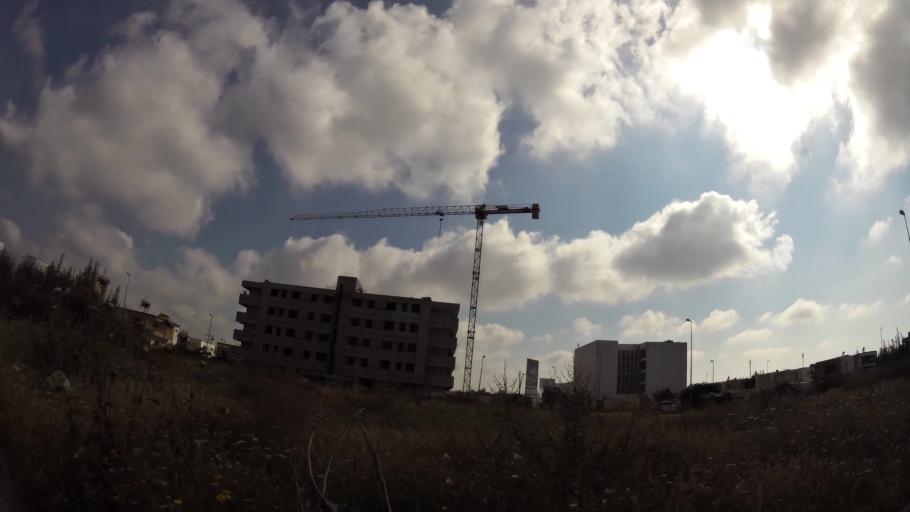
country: MA
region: Rabat-Sale-Zemmour-Zaer
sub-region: Skhirate-Temara
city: Temara
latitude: 33.9512
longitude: -6.8770
